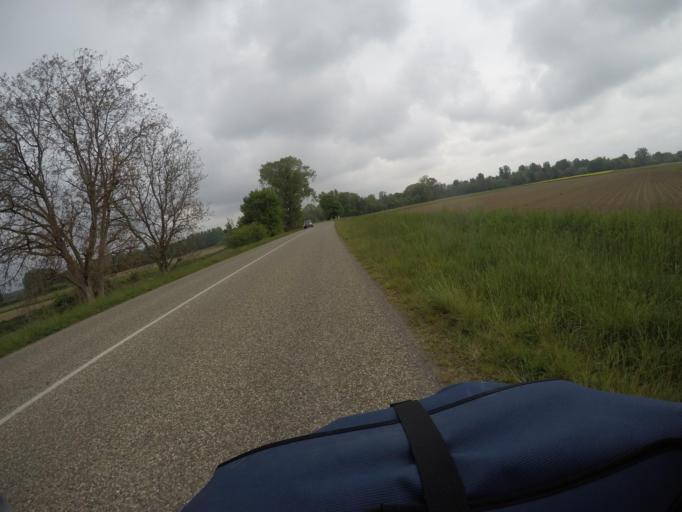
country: FR
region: Alsace
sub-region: Departement du Bas-Rhin
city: Drusenheim
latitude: 48.7727
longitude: 7.9619
